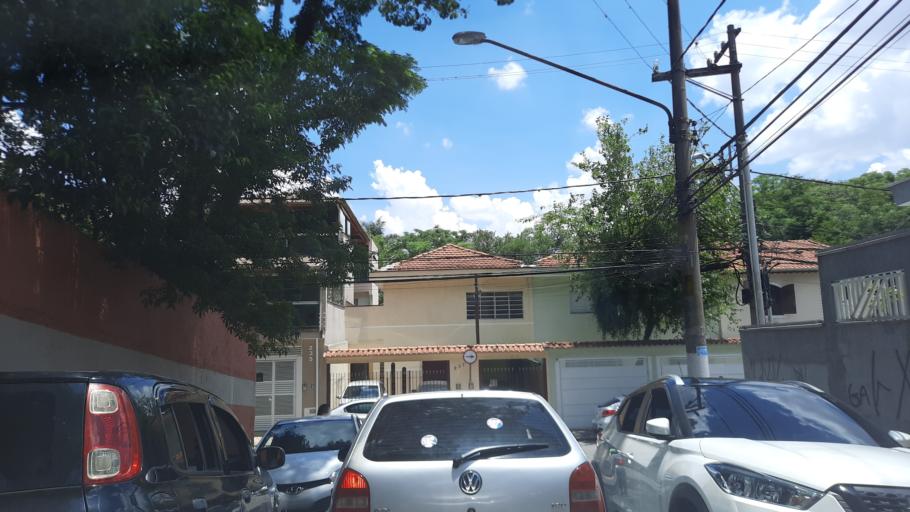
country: BR
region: Sao Paulo
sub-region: Sao Paulo
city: Sao Paulo
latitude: -23.4913
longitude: -46.6815
